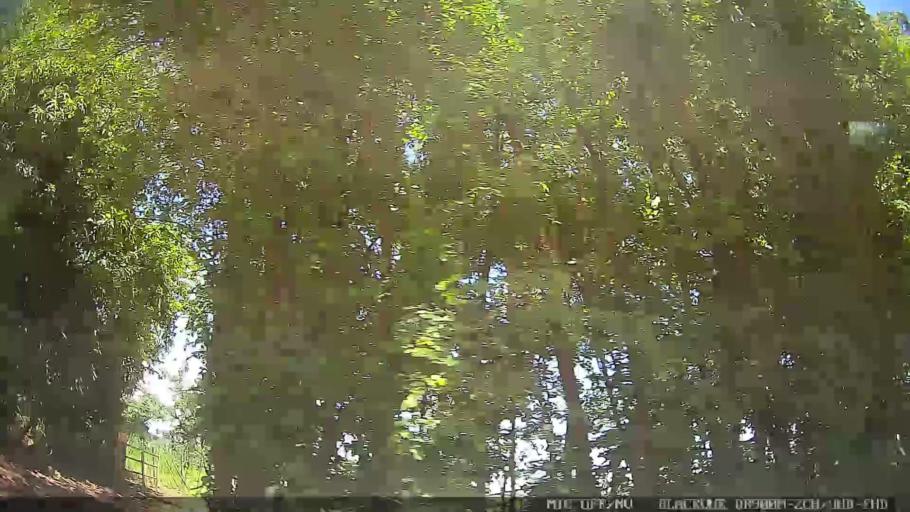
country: BR
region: Sao Paulo
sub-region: Jaguariuna
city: Jaguariuna
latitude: -22.7232
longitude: -46.9999
